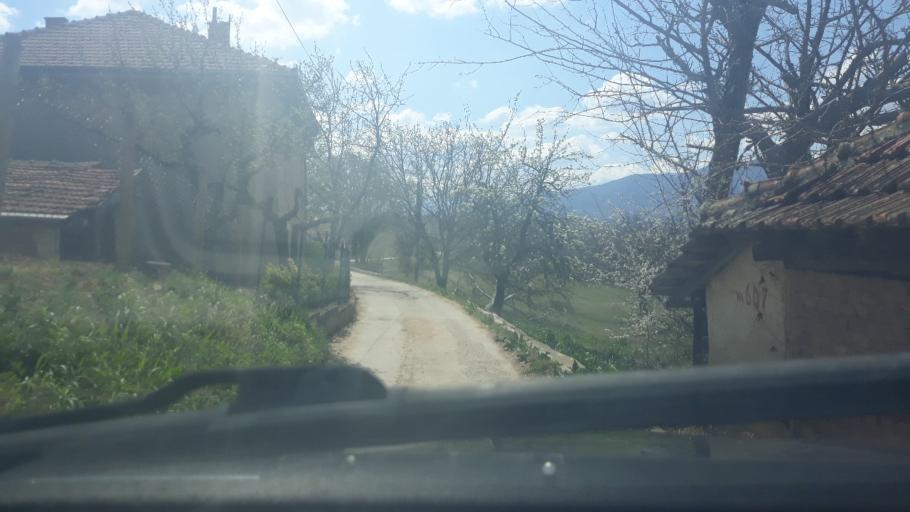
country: MK
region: Caska
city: Caska
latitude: 41.6479
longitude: 21.6945
